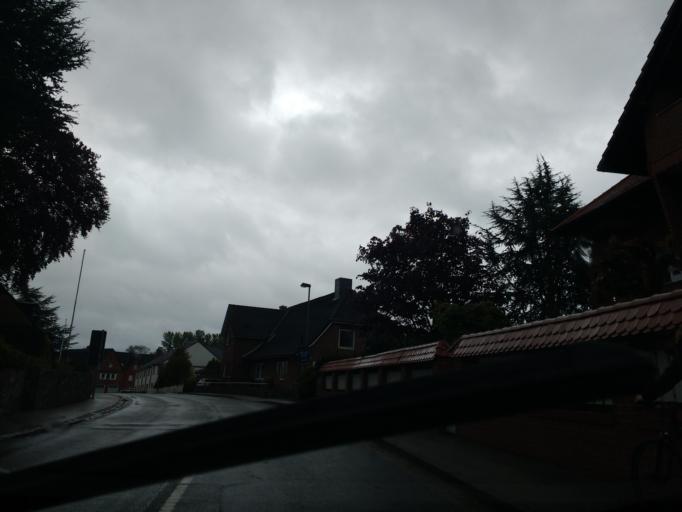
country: DE
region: Schleswig-Holstein
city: Loose
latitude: 54.5201
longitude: 9.8870
